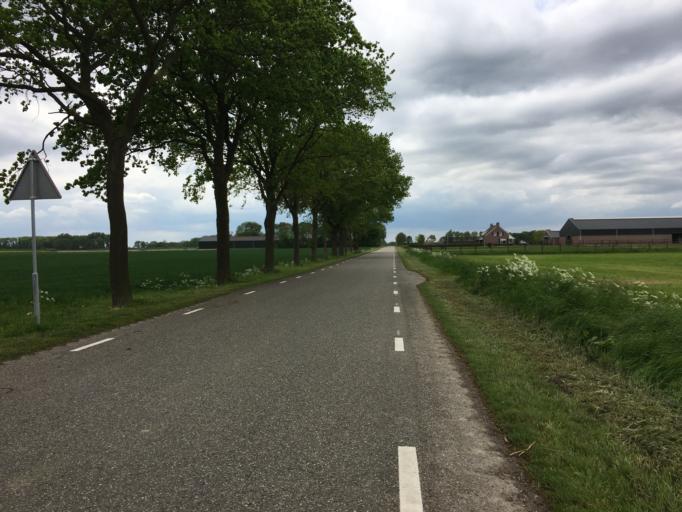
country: NL
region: Gelderland
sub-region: Gemeente Zaltbommel
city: Nederhemert-Noord
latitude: 51.7243
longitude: 5.2025
